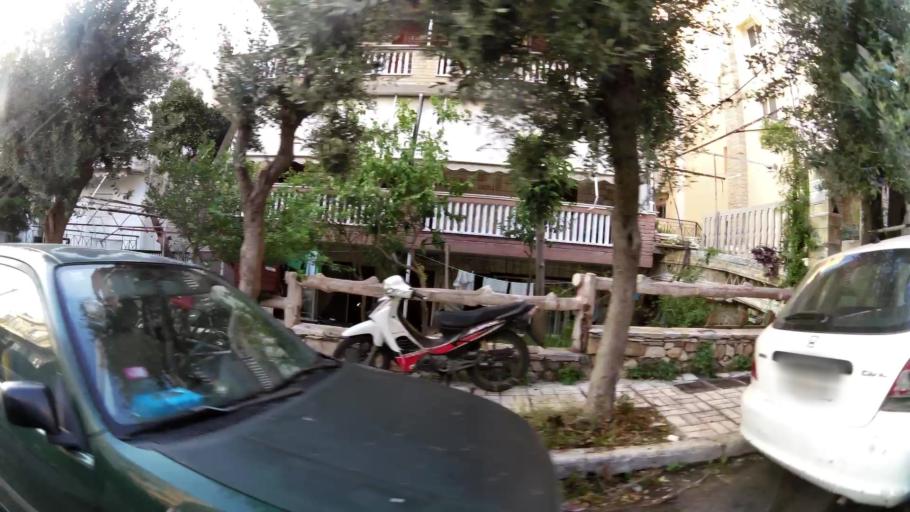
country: GR
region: Attica
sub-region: Nomarchia Athinas
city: Glyfada
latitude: 37.8858
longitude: 23.7709
